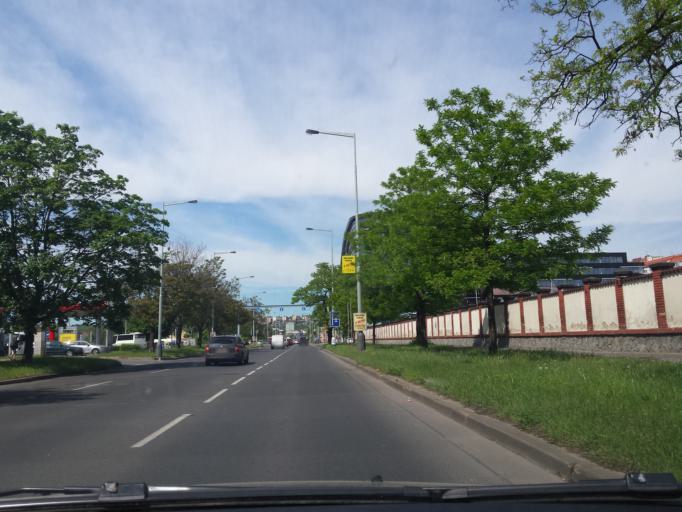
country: CZ
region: Praha
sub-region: Praha 8
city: Karlin
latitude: 50.0993
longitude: 14.4433
